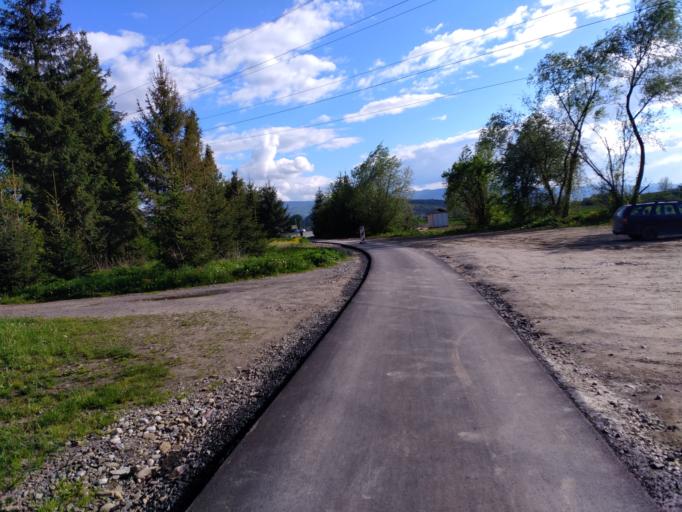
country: PL
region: Lesser Poland Voivodeship
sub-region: Powiat nowosadecki
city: Stary Sacz
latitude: 49.5839
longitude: 20.6390
